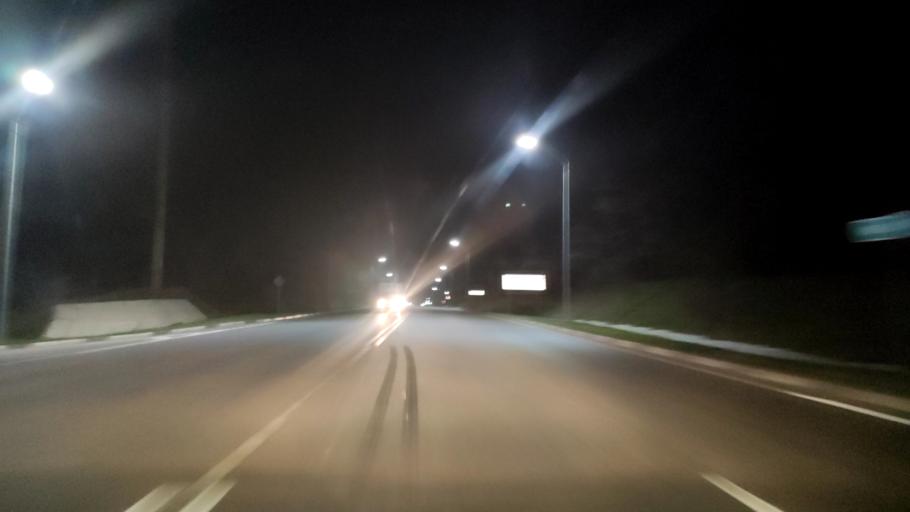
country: RU
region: Belgorod
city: Staryy Oskol
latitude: 51.3570
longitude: 37.8339
